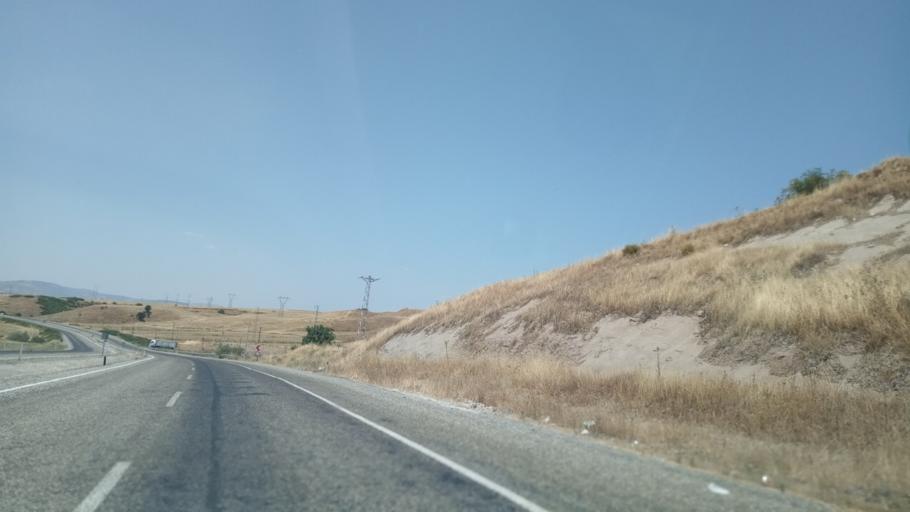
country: TR
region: Batman
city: Bekirhan
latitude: 38.1582
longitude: 41.3424
